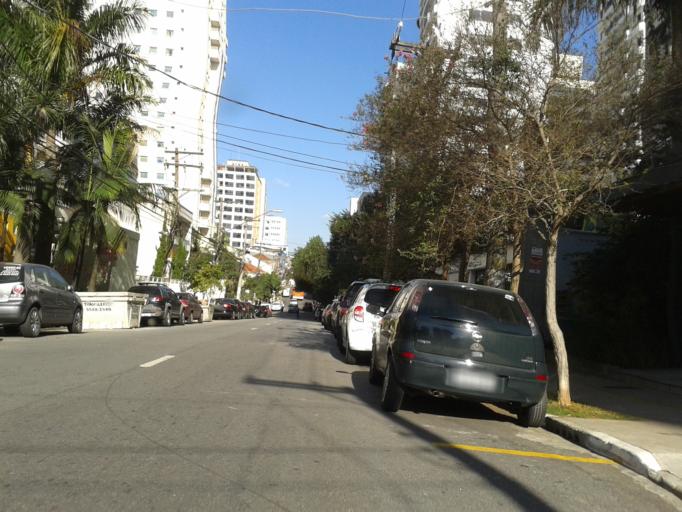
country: BR
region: Sao Paulo
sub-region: Sao Paulo
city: Sao Paulo
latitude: -23.5546
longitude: -46.6762
